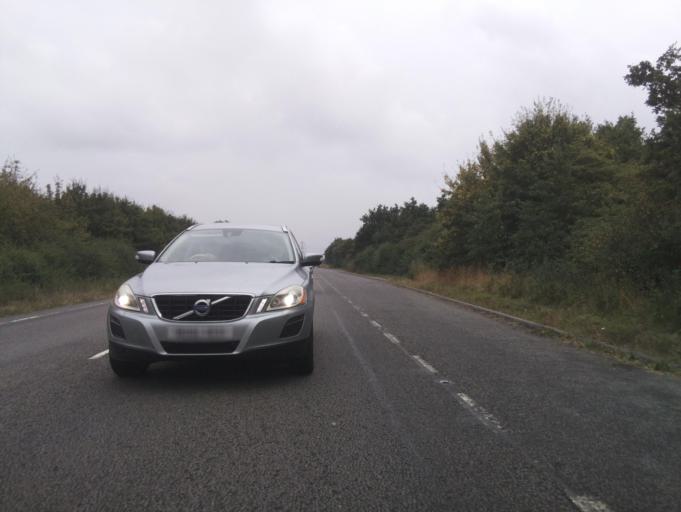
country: GB
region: England
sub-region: Nottinghamshire
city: South Collingham
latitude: 53.0899
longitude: -0.7614
